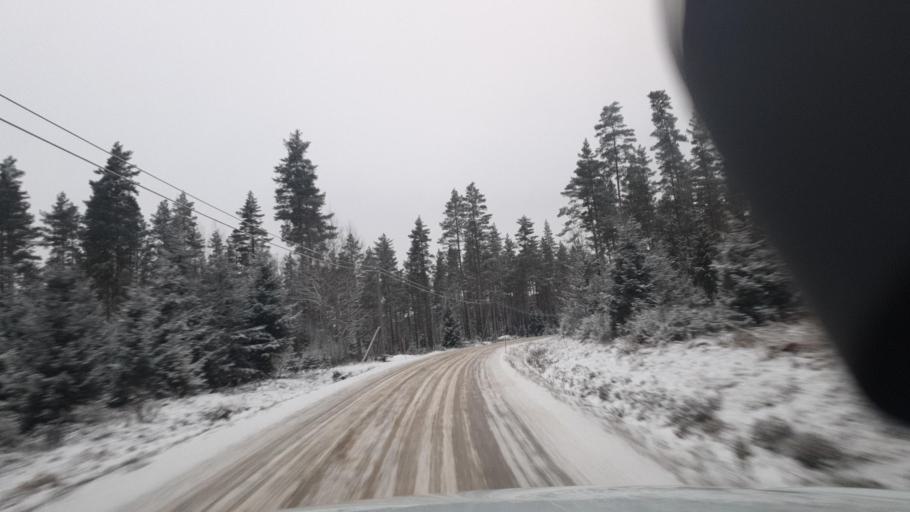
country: SE
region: Vaermland
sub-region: Eda Kommun
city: Charlottenberg
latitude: 59.9787
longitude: 12.4901
